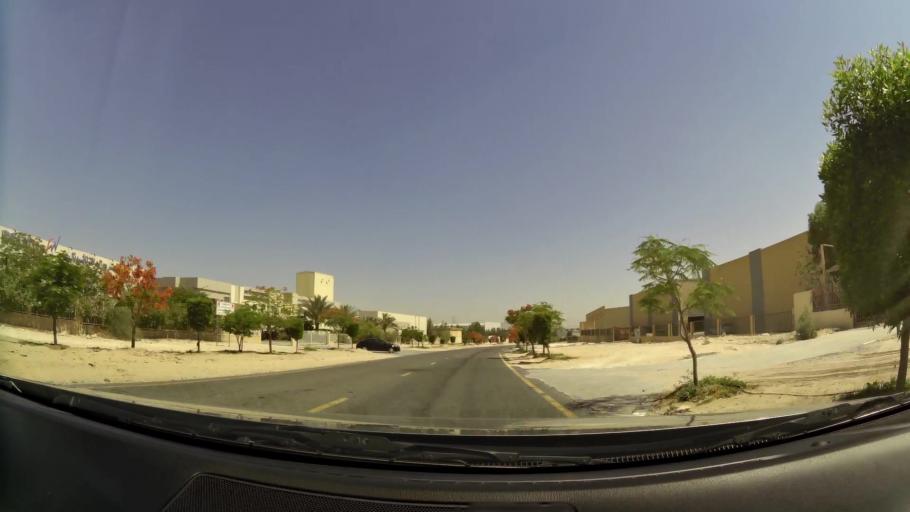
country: AE
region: Dubai
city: Dubai
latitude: 24.9818
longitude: 55.2073
